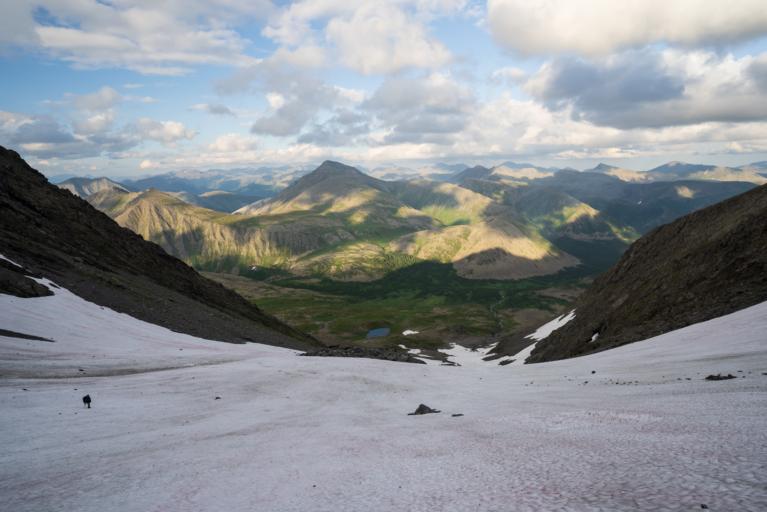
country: RU
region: Komi Republic
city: Synya
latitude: 64.8272
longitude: 59.2960
